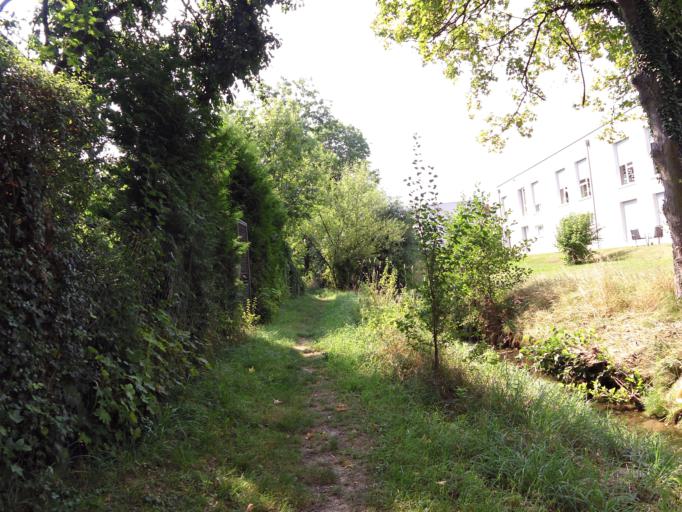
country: DE
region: Bavaria
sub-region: Regierungsbezirk Unterfranken
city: Estenfeld
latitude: 49.8243
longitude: 10.0075
